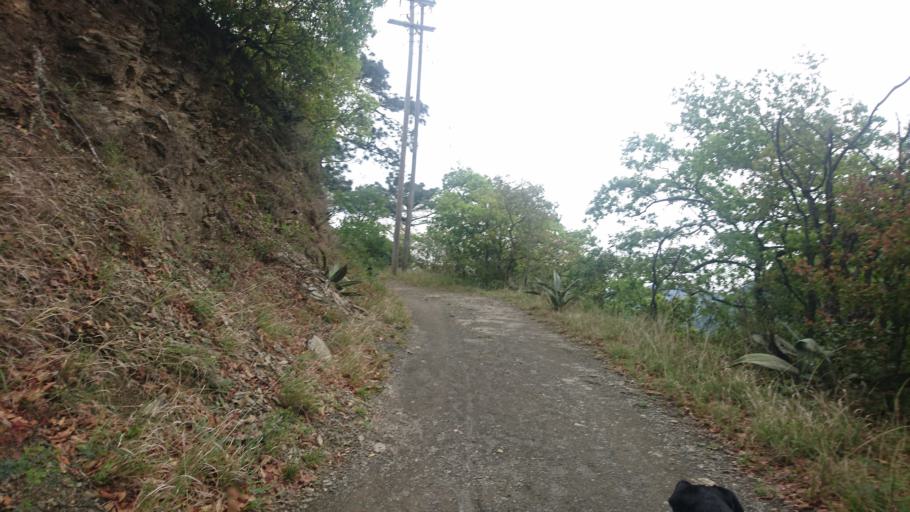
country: MX
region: Nuevo Leon
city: Garza Garcia
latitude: 25.6051
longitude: -100.3401
